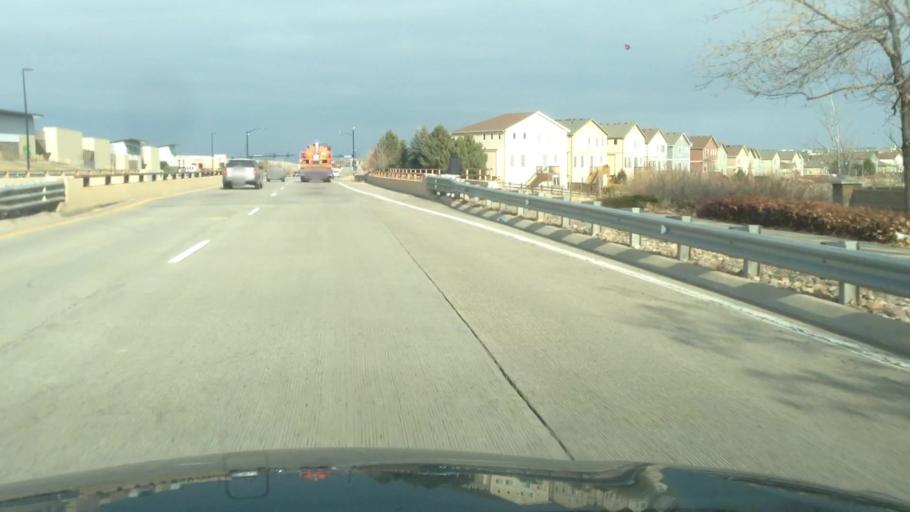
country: US
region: Colorado
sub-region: Arapahoe County
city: Dove Valley
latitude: 39.5717
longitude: -104.8051
